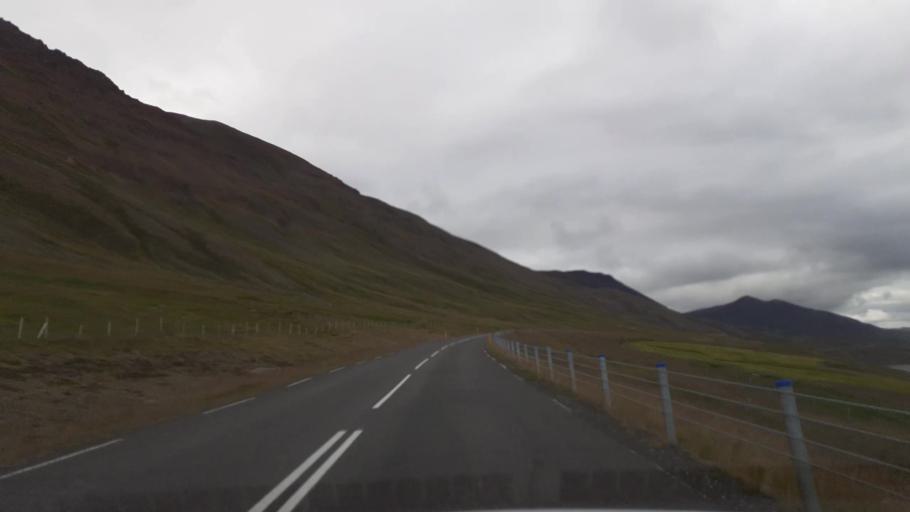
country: IS
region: Northeast
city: Akureyri
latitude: 65.8597
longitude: -18.0657
